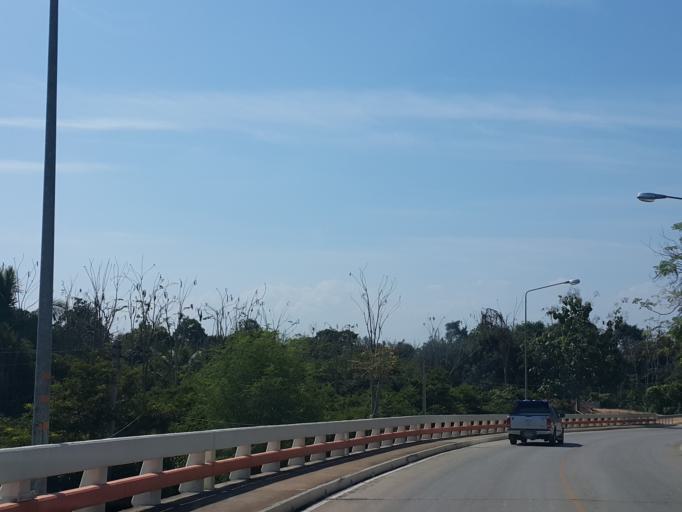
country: TH
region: Sukhothai
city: Si Samrong
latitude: 17.2234
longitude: 99.8577
